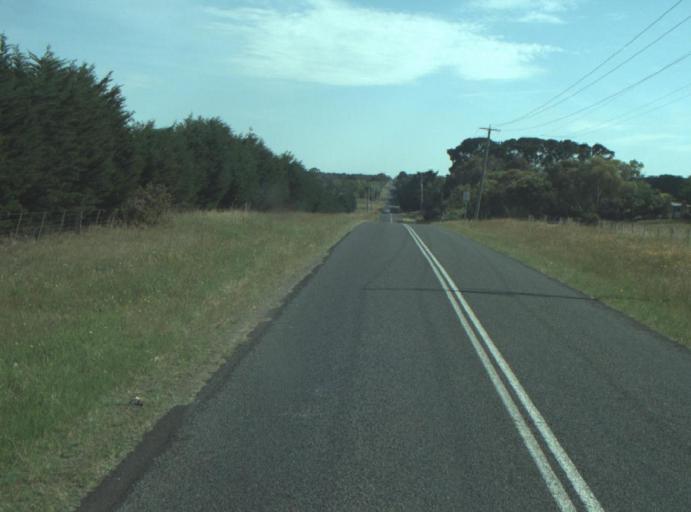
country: AU
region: Victoria
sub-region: Greater Geelong
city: Leopold
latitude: -38.2001
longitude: 144.5093
